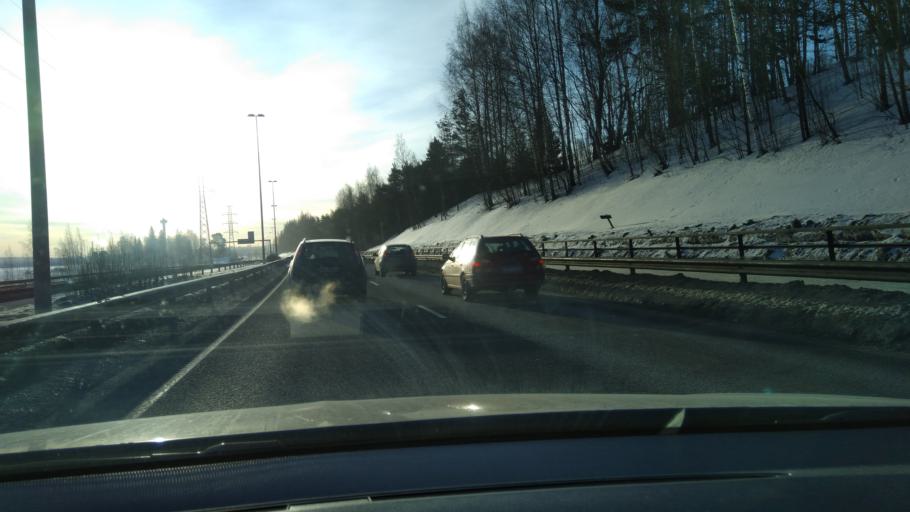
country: FI
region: Pirkanmaa
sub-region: Tampere
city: Pirkkala
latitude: 61.5091
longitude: 23.6931
